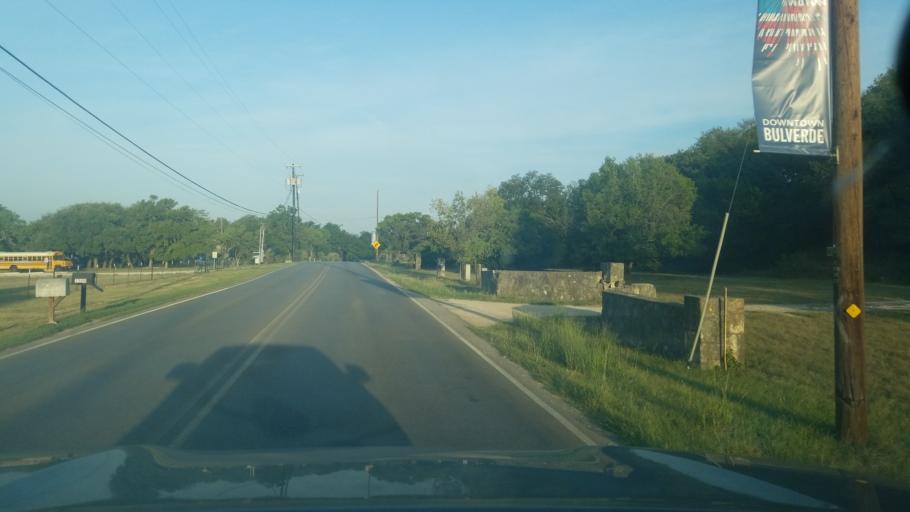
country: US
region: Texas
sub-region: Comal County
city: Bulverde
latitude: 29.7428
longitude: -98.4479
